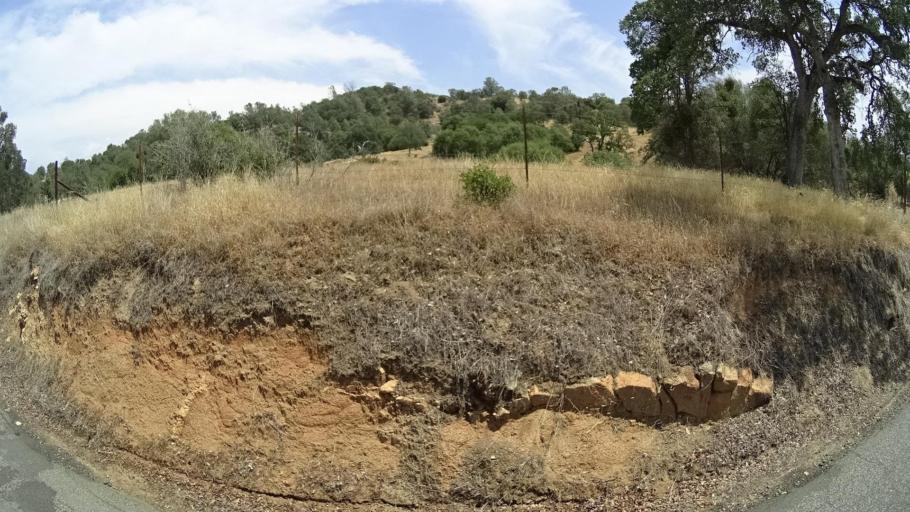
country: US
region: California
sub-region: Mariposa County
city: Mariposa
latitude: 37.3939
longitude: -119.8761
